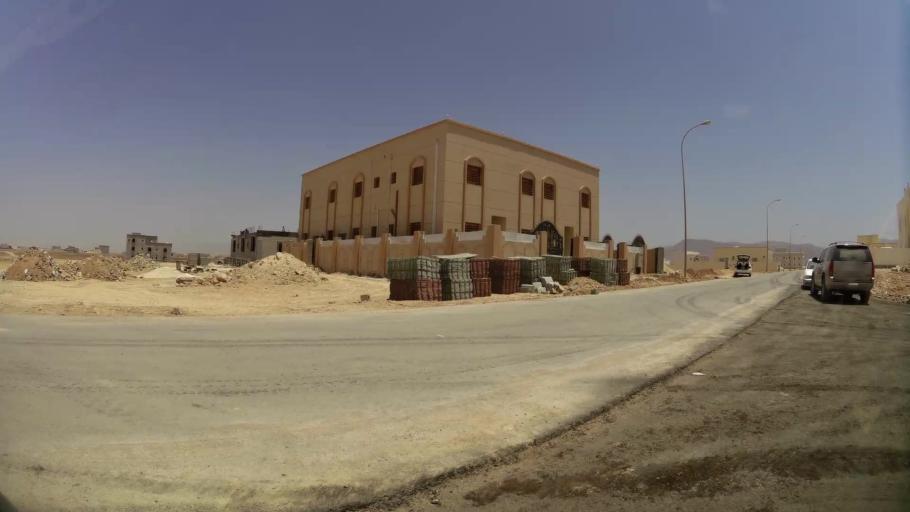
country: OM
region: Zufar
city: Salalah
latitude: 17.0992
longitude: 54.2056
